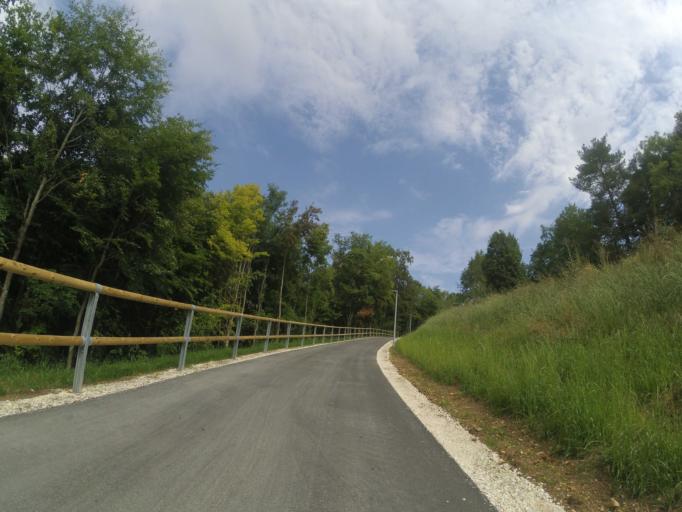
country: DE
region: Baden-Wuerttemberg
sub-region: Tuebingen Region
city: Dornstadt
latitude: 48.4274
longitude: 9.8995
